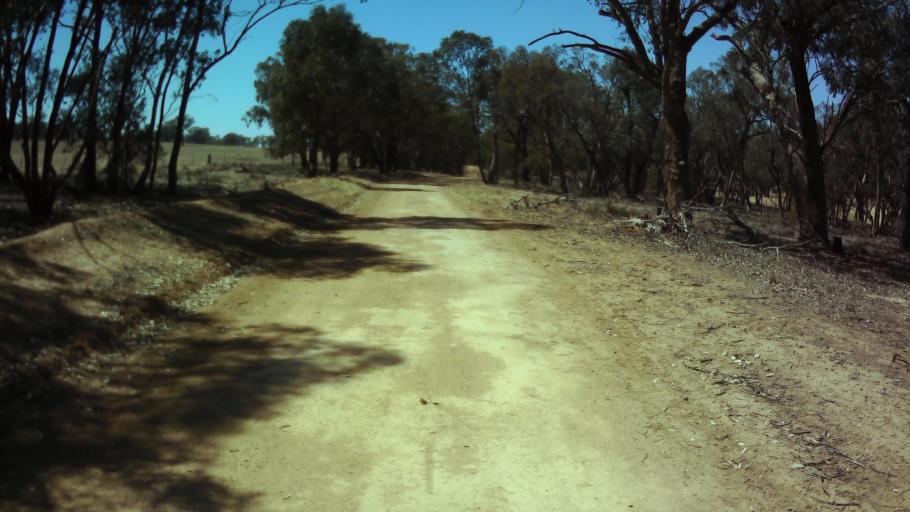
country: AU
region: New South Wales
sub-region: Weddin
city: Grenfell
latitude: -33.9583
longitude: 148.0858
